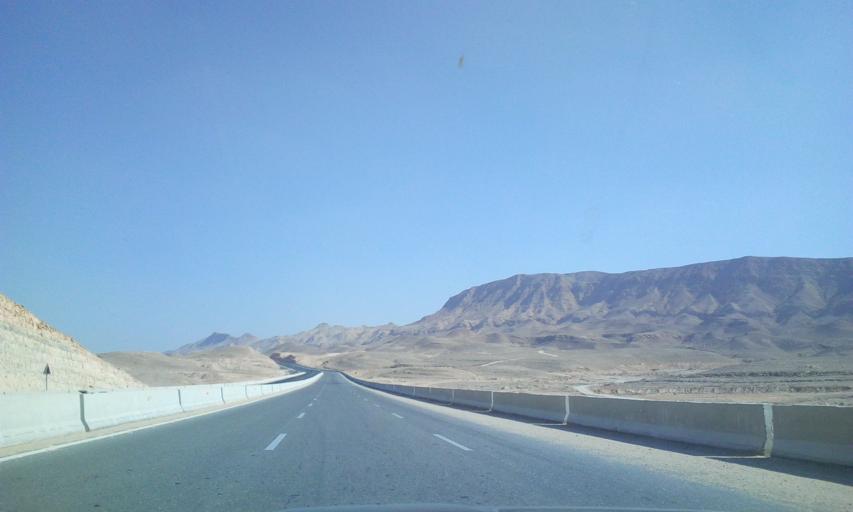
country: EG
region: As Suways
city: Ain Sukhna
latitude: 29.4672
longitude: 32.3246
